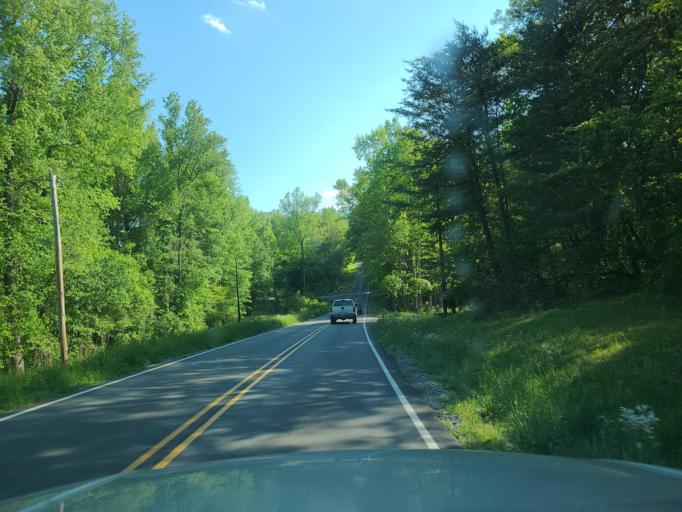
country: US
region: North Carolina
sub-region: Cleveland County
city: Shelby
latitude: 35.2358
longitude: -81.5279
